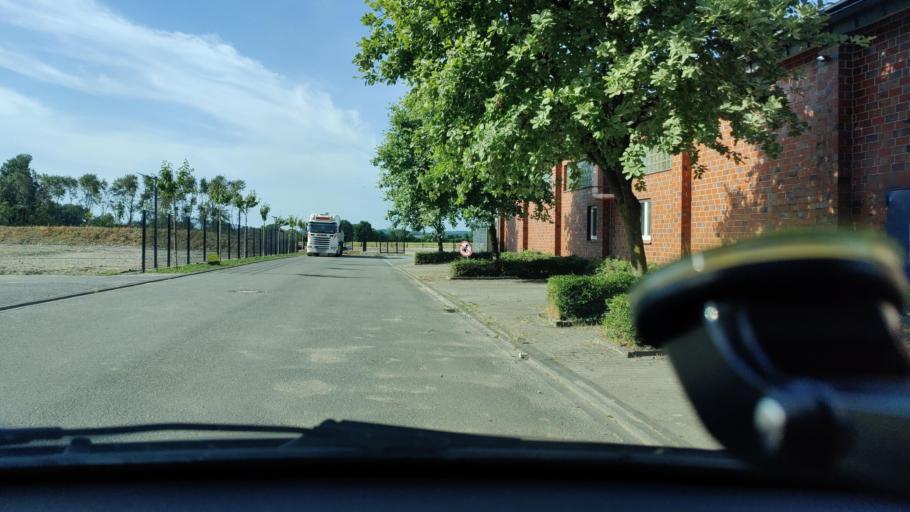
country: DE
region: North Rhine-Westphalia
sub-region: Regierungsbezirk Munster
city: Billerbeck
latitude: 52.0280
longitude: 7.2802
